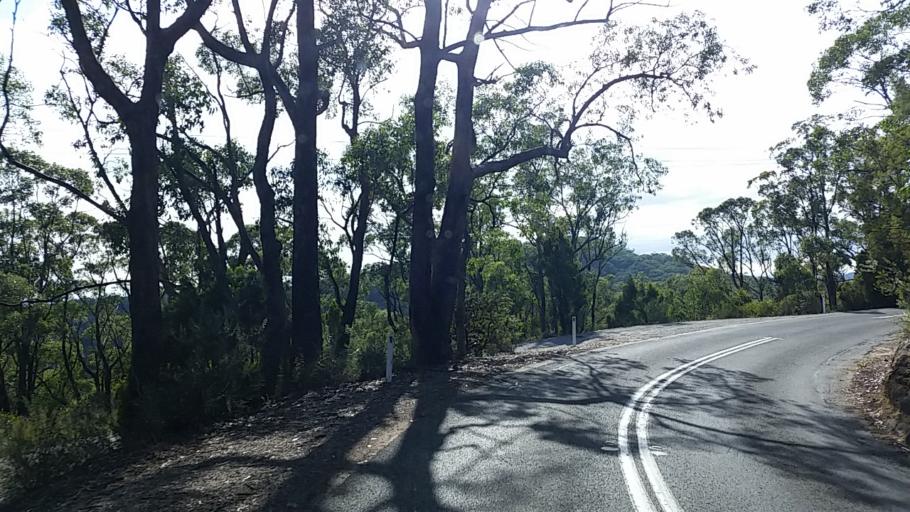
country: AU
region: South Australia
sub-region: Adelaide Hills
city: Crafers
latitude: -34.9723
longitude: 138.7078
